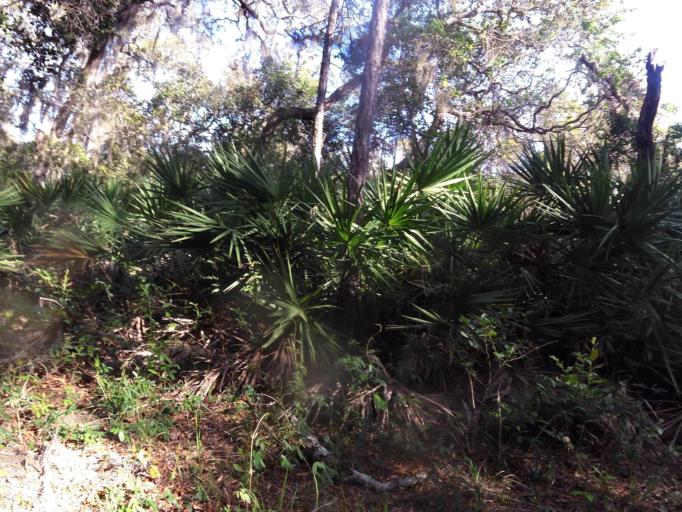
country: US
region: Florida
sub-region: Saint Johns County
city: Villano Beach
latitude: 30.0171
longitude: -81.3378
